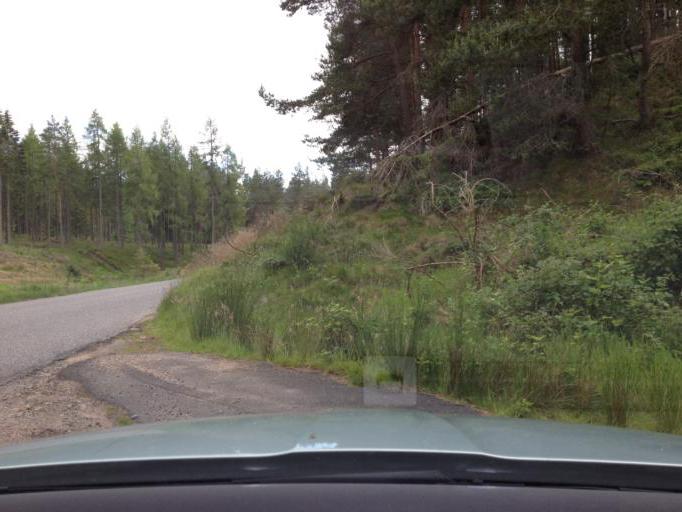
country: GB
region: Scotland
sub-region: Aberdeenshire
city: Banchory
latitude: 56.9975
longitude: -2.5727
